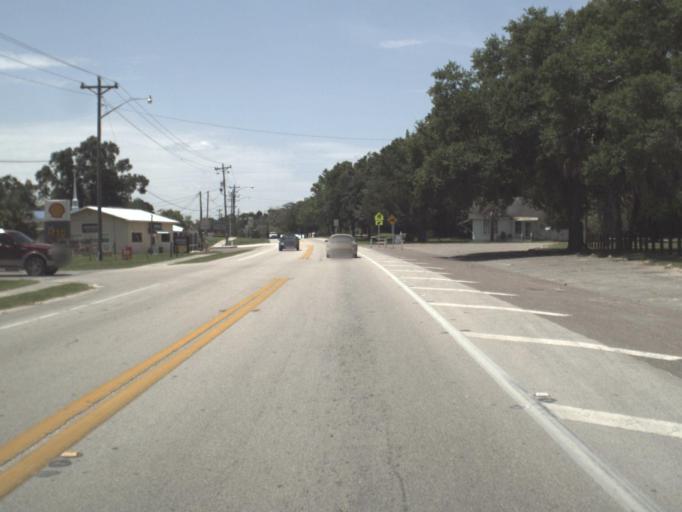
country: US
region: Florida
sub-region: Gilchrist County
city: Trenton
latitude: 29.7515
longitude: -82.8607
